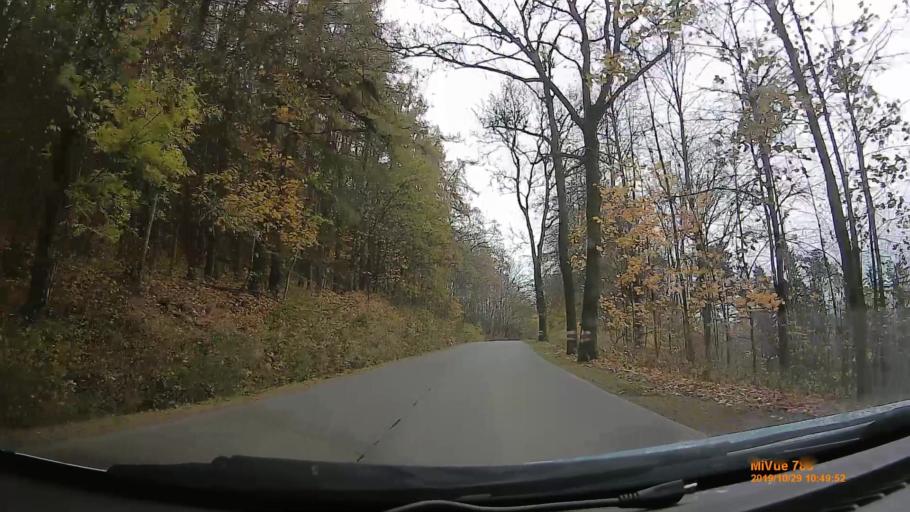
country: PL
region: Lower Silesian Voivodeship
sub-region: Powiat klodzki
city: Nowa Ruda
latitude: 50.5488
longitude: 16.4586
